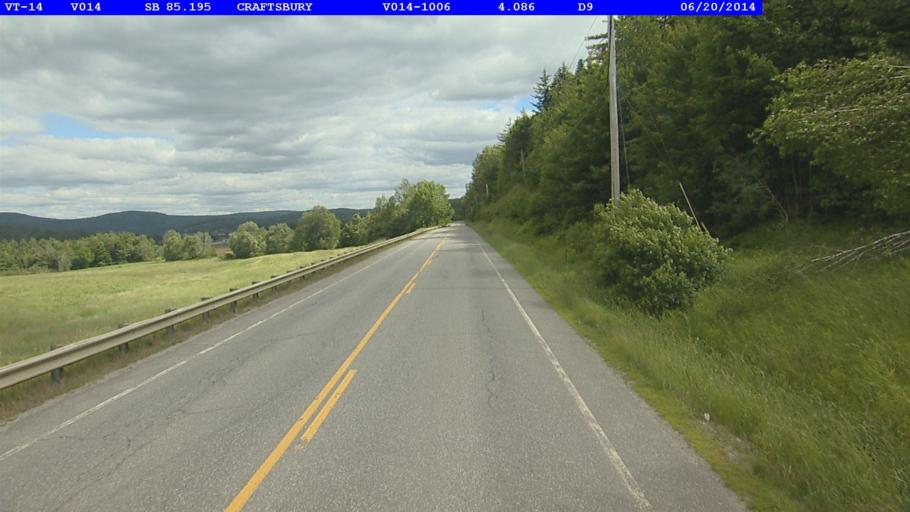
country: US
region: Vermont
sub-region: Caledonia County
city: Hardwick
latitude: 44.6497
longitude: -72.4050
